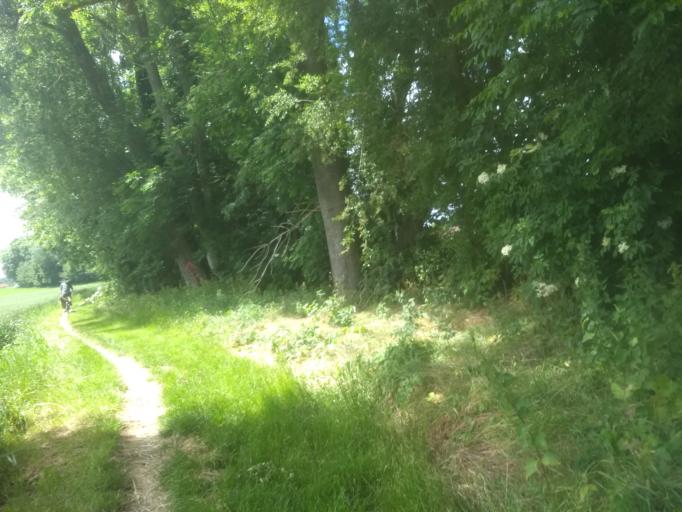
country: FR
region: Nord-Pas-de-Calais
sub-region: Departement du Pas-de-Calais
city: Agny
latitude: 50.2524
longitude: 2.7353
